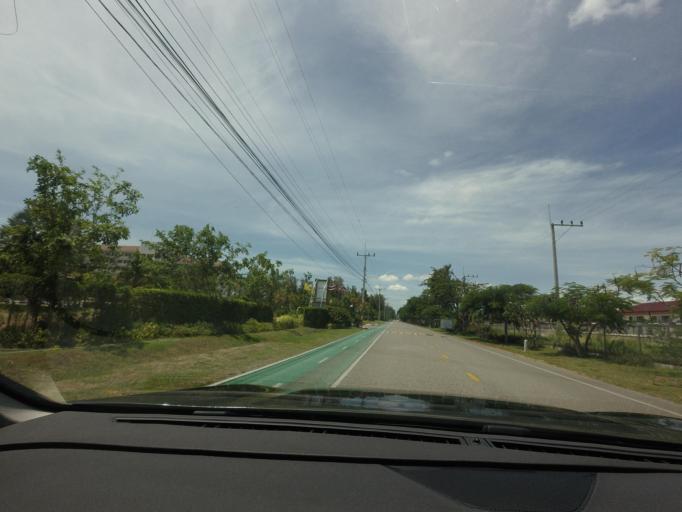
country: TH
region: Prachuap Khiri Khan
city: Hua Hin
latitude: 12.5034
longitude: 99.9727
